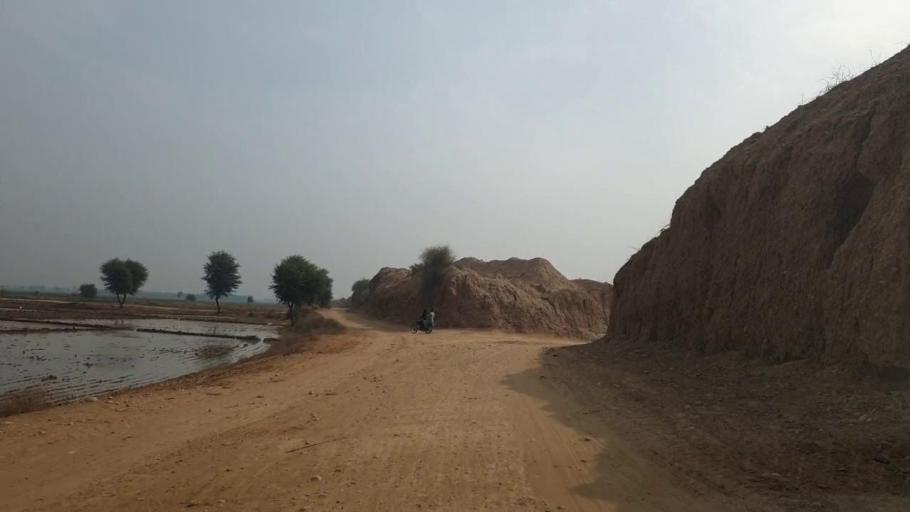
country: PK
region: Sindh
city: Sann
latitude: 26.0159
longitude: 68.1449
